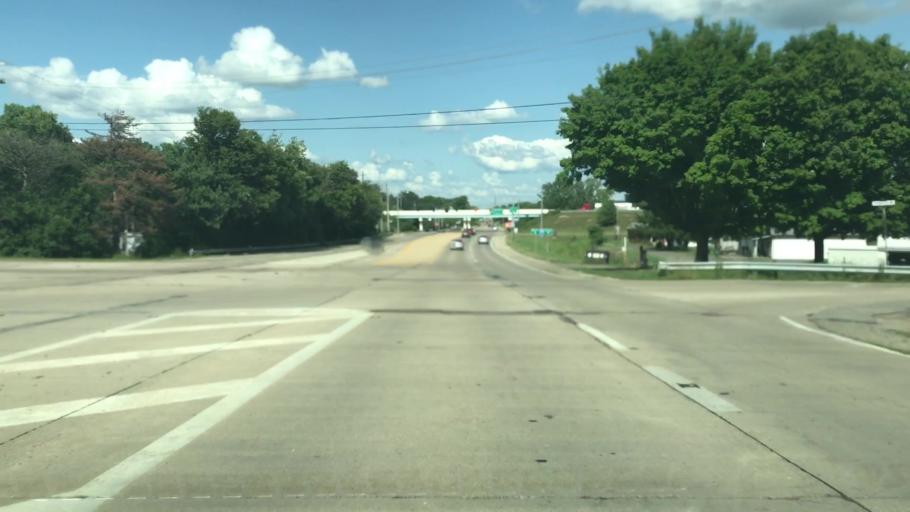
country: US
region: Ohio
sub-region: Clark County
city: Holiday Valley
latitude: 39.8438
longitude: -83.9965
